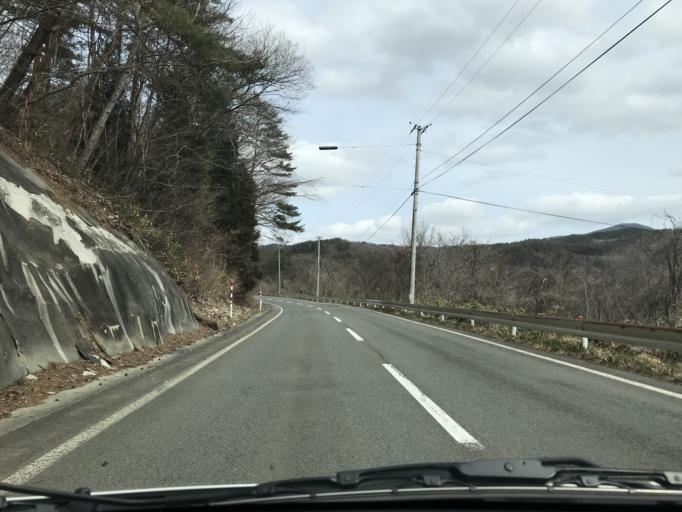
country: JP
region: Iwate
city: Tono
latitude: 39.3049
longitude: 141.3696
